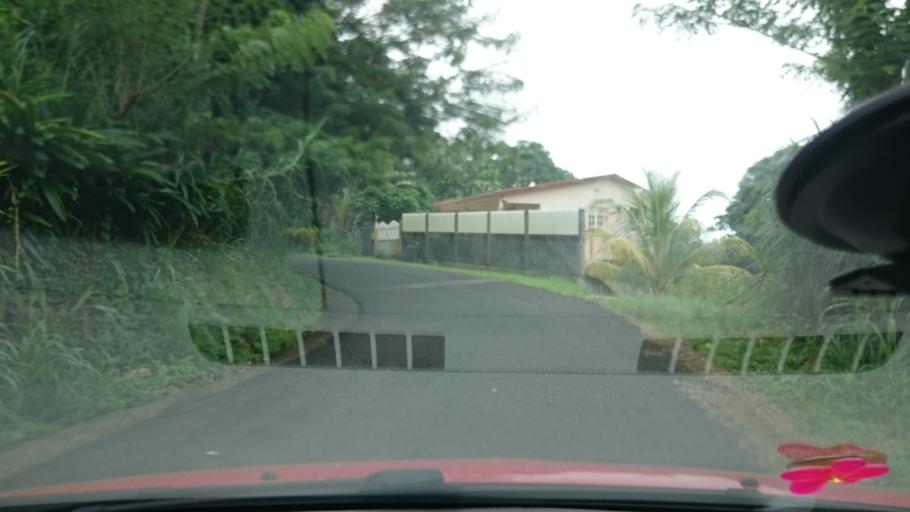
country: MQ
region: Martinique
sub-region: Martinique
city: Riviere-Pilote
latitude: 14.4959
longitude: -60.9234
